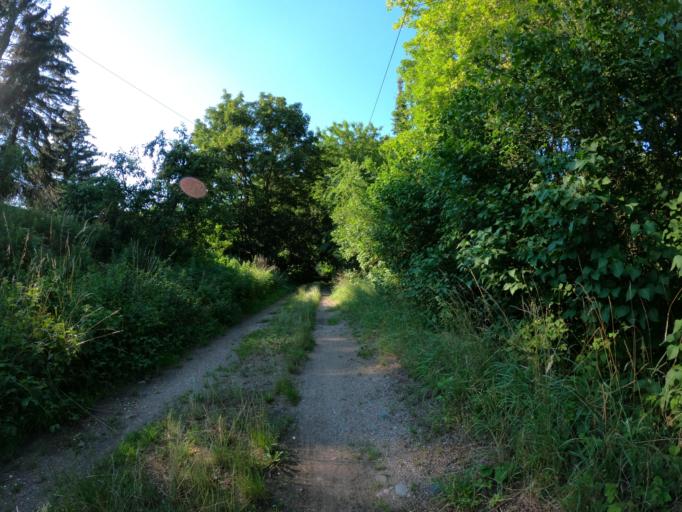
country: DE
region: Brandenburg
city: Tantow
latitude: 53.2377
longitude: 14.3652
